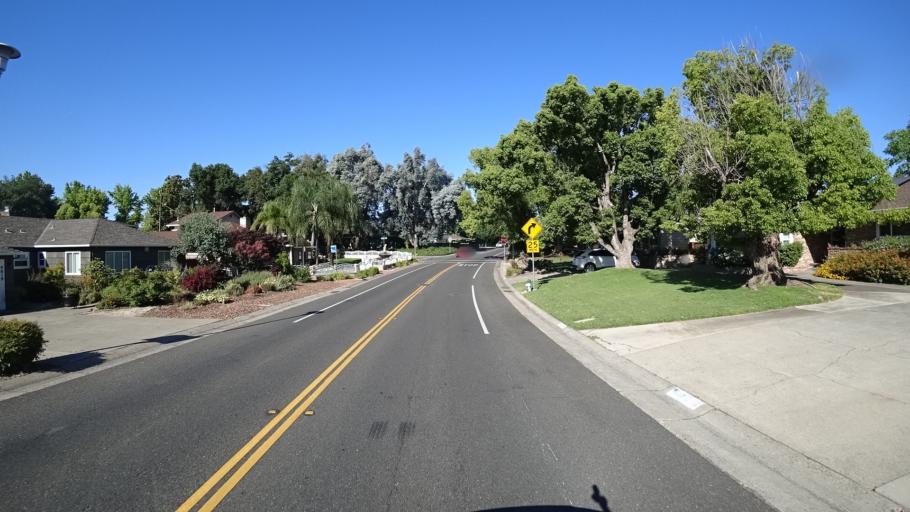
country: US
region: California
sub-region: Sacramento County
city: Sacramento
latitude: 38.5303
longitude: -121.5088
